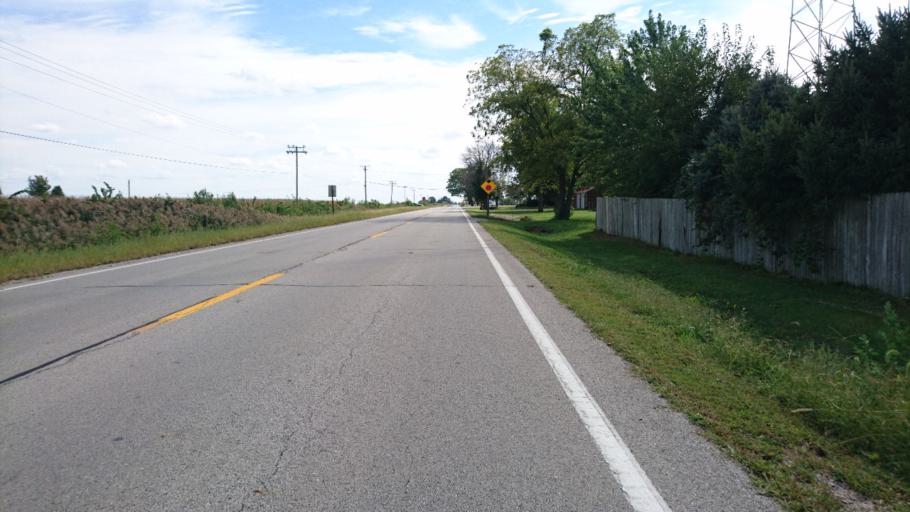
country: US
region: Illinois
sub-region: Grundy County
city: Gardner
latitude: 41.1875
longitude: -88.3012
